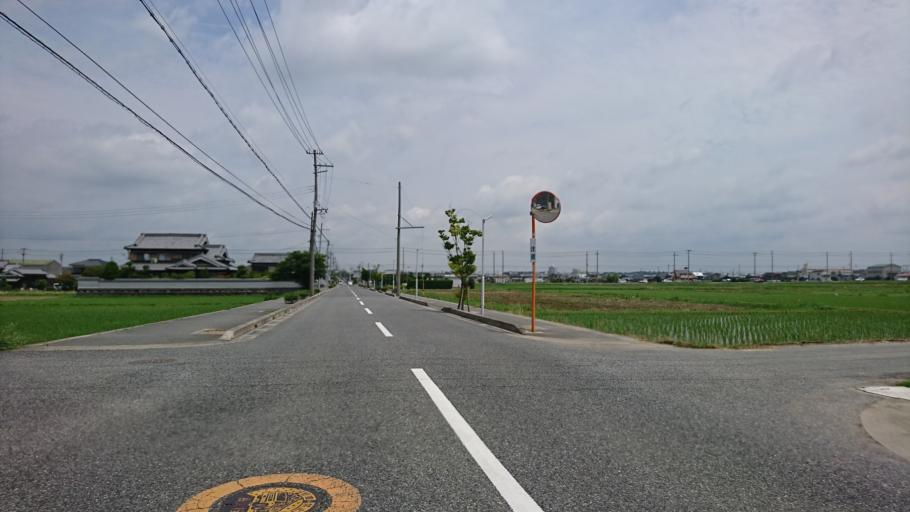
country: JP
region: Hyogo
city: Kakogawacho-honmachi
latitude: 34.7316
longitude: 134.9122
